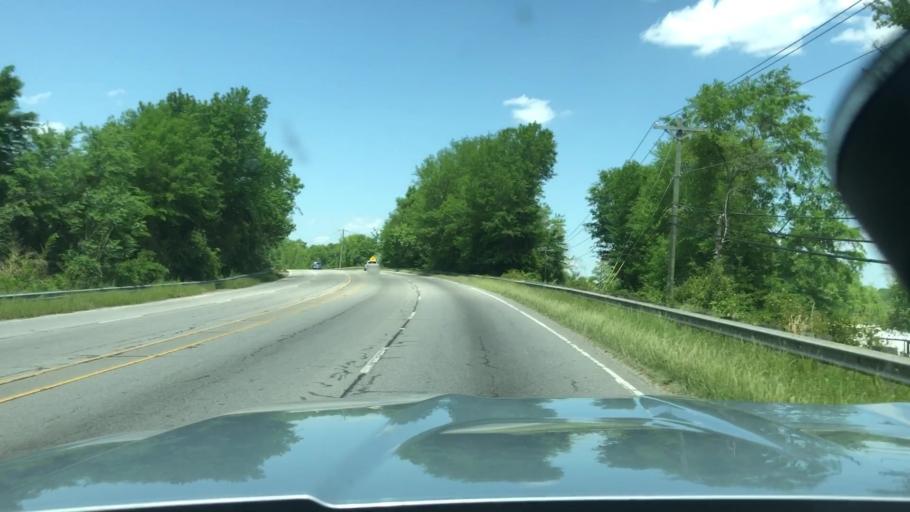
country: US
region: South Carolina
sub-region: Lexington County
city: Pineridge
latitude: 33.9075
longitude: -81.0661
